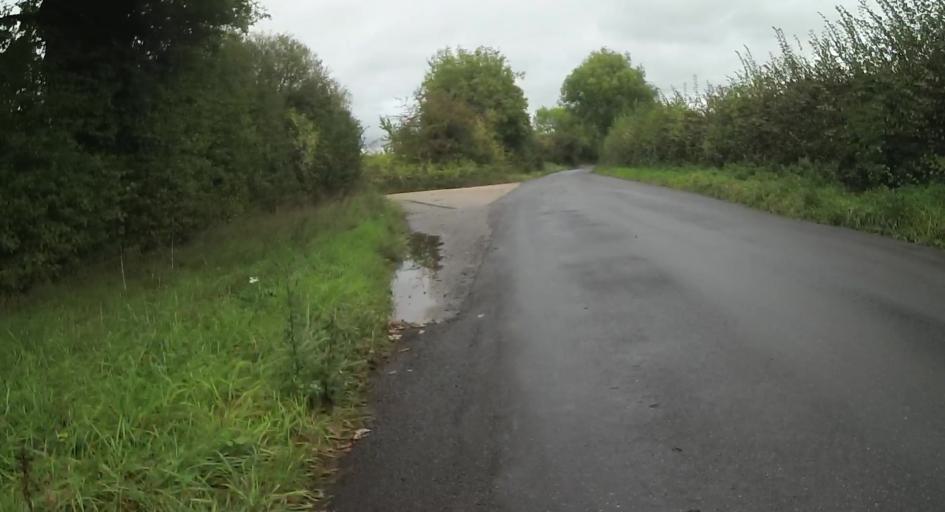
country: GB
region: England
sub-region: Hampshire
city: Tadley
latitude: 51.3864
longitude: -1.1792
